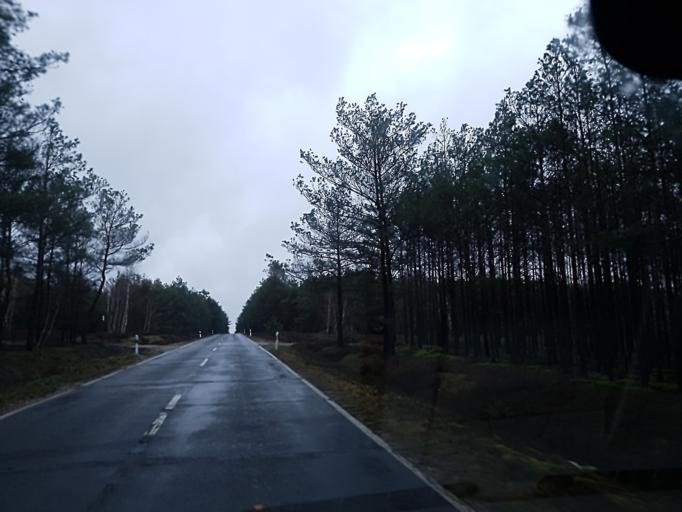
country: DE
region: Brandenburg
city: Schonewalde
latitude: 51.6136
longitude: 13.6343
